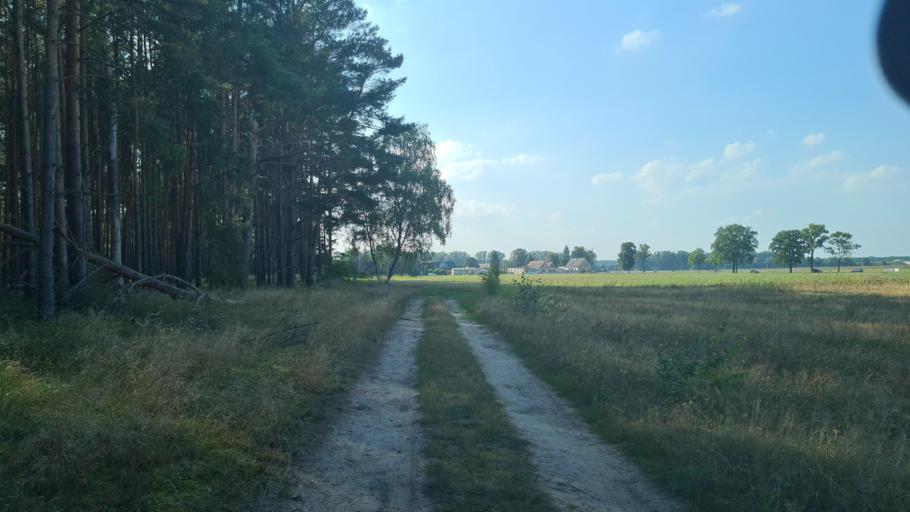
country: DE
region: Brandenburg
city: Luckenwalde
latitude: 52.1128
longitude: 13.2148
